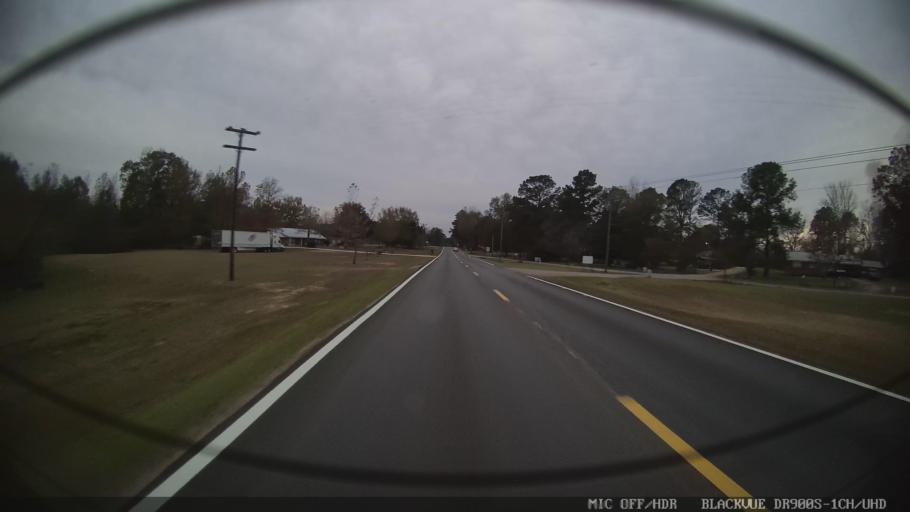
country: US
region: Mississippi
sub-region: Clarke County
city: Quitman
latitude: 32.0528
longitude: -88.6886
